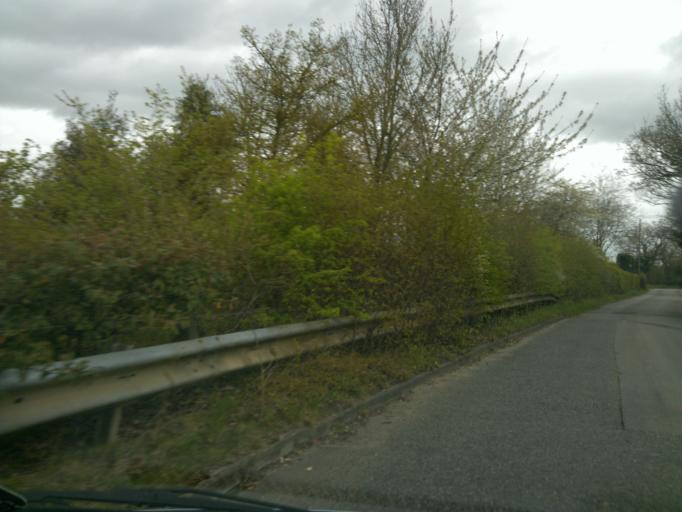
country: GB
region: England
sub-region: Essex
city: Wivenhoe
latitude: 51.8650
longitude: 0.9771
